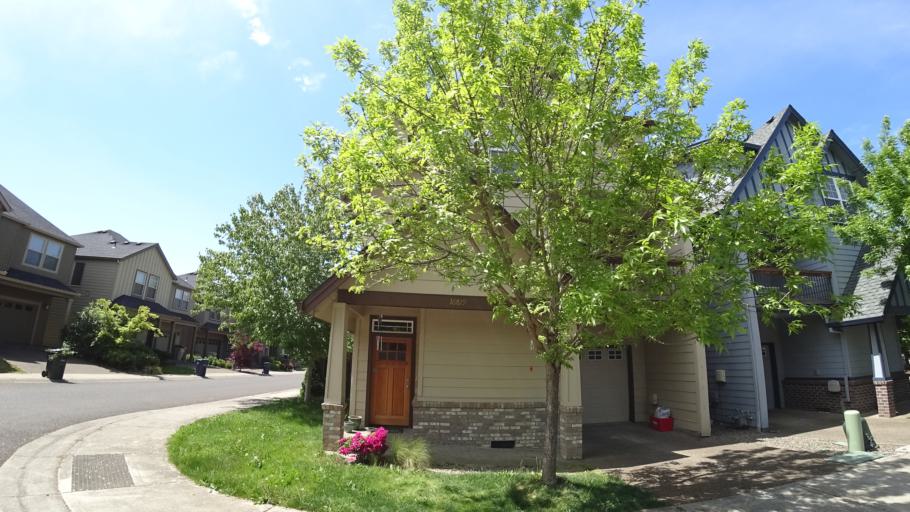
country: US
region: Oregon
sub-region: Washington County
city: Aloha
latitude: 45.4881
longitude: -122.8502
